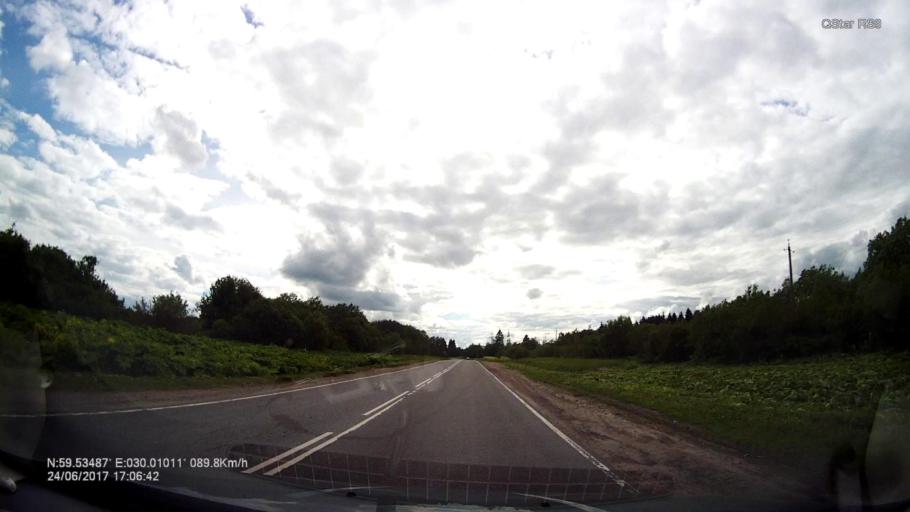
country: RU
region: Leningrad
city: Voyskovitsy
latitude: 59.5348
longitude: 30.0091
